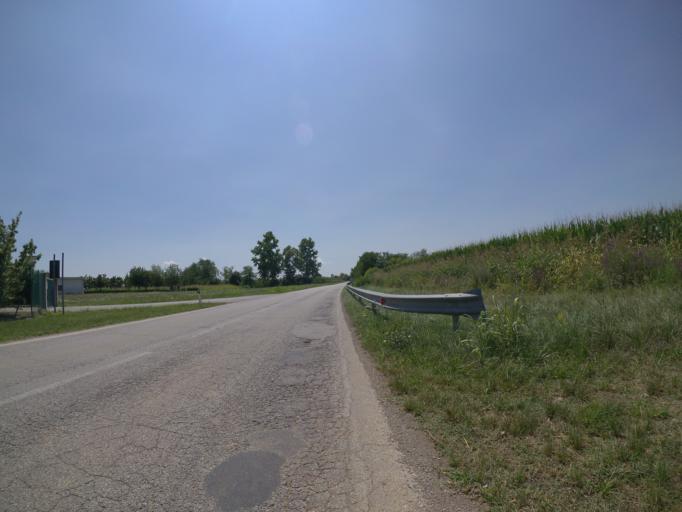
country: IT
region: Friuli Venezia Giulia
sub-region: Provincia di Udine
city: Lestizza
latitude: 45.9652
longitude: 13.1409
